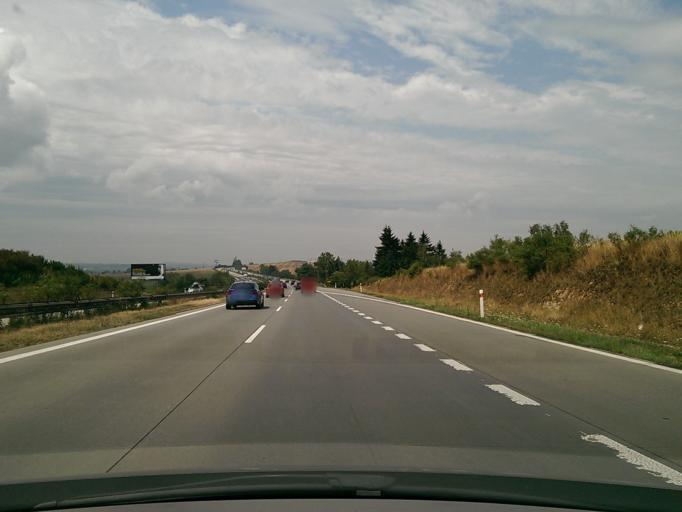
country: CZ
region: Vysocina
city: Merin
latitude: 49.3875
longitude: 15.9191
